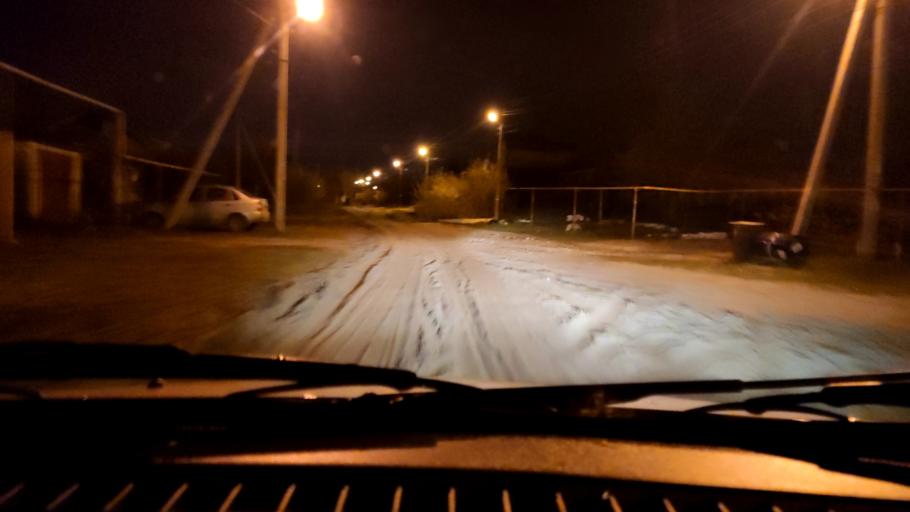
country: RU
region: Voronezj
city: Pridonskoy
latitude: 51.7021
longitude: 39.0830
